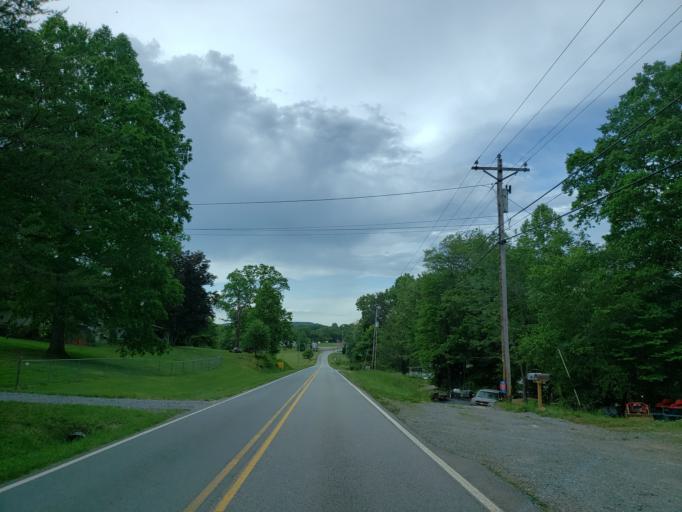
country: US
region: Georgia
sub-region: Fannin County
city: Blue Ridge
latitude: 34.8667
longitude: -84.3692
